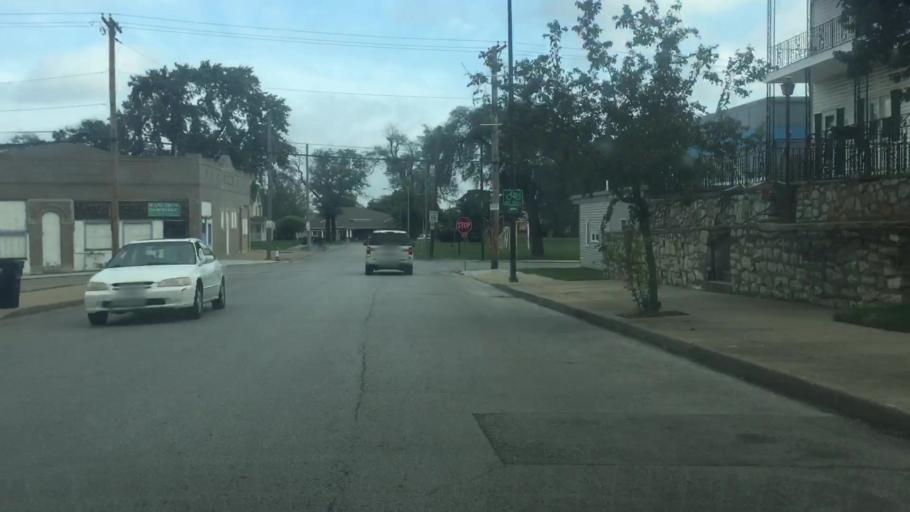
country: US
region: Missouri
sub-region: Jackson County
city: Kansas City
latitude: 39.1105
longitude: -94.5699
